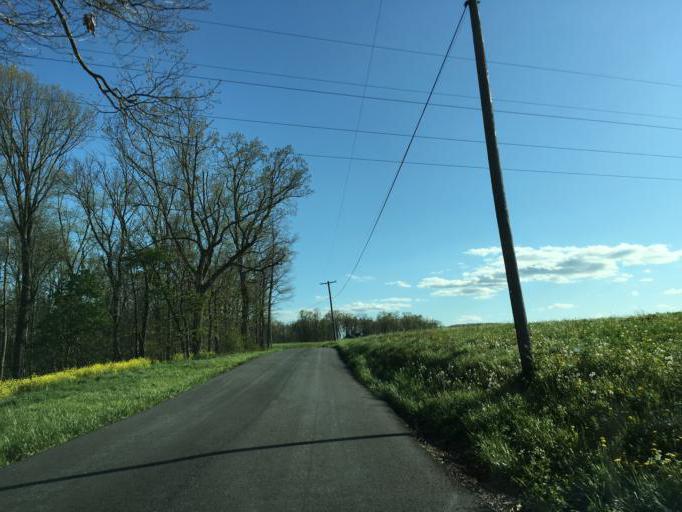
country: US
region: Maryland
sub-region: Frederick County
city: Woodsboro
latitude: 39.5750
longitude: -77.2366
